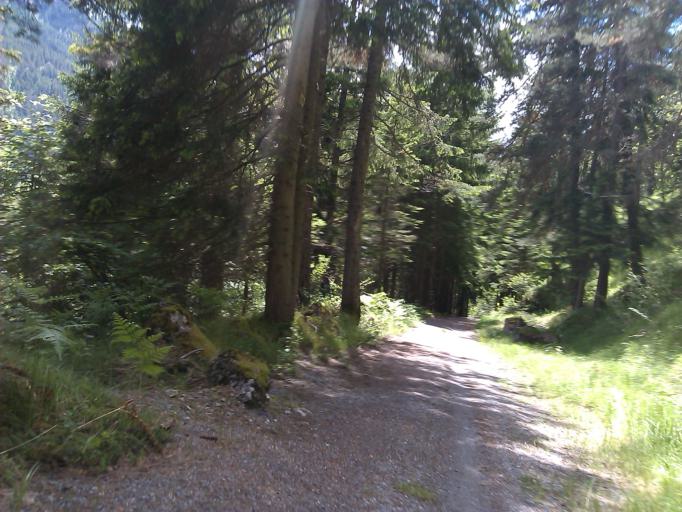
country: AT
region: Tyrol
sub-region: Politischer Bezirk Imst
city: Nassereith
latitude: 47.3507
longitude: 10.8232
